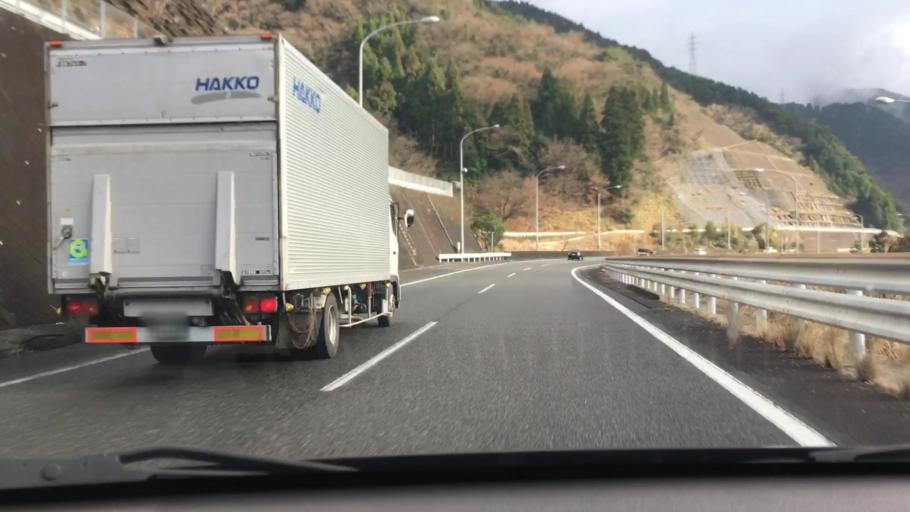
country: JP
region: Kumamoto
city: Yatsushiro
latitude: 32.4005
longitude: 130.7006
